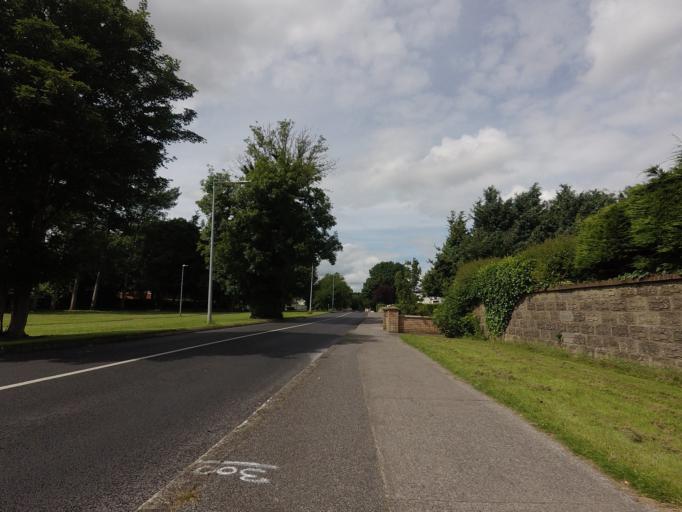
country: IE
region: Leinster
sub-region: Fingal County
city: Blanchardstown
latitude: 53.3800
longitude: -6.3925
